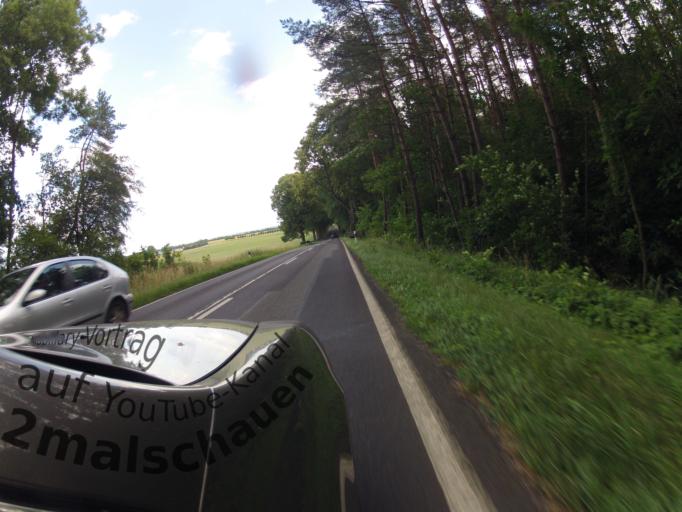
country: DE
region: Mecklenburg-Vorpommern
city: Usedom
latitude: 53.9053
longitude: 14.0360
